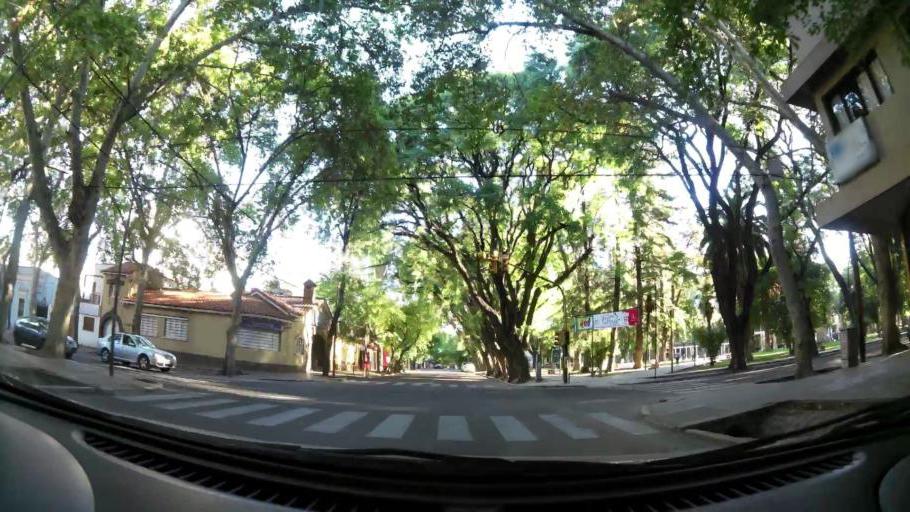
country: AR
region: Mendoza
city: Mendoza
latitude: -32.8913
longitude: -68.8477
